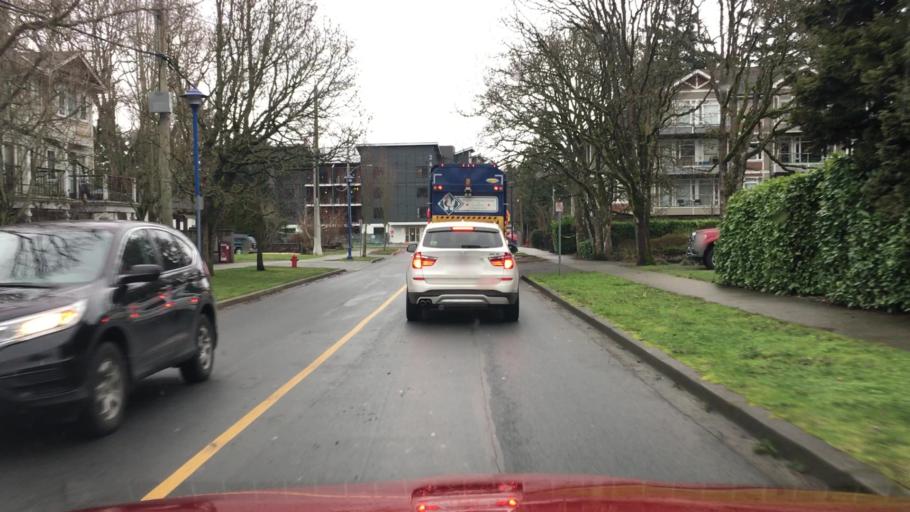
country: CA
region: British Columbia
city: Langford
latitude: 48.4532
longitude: -123.4999
